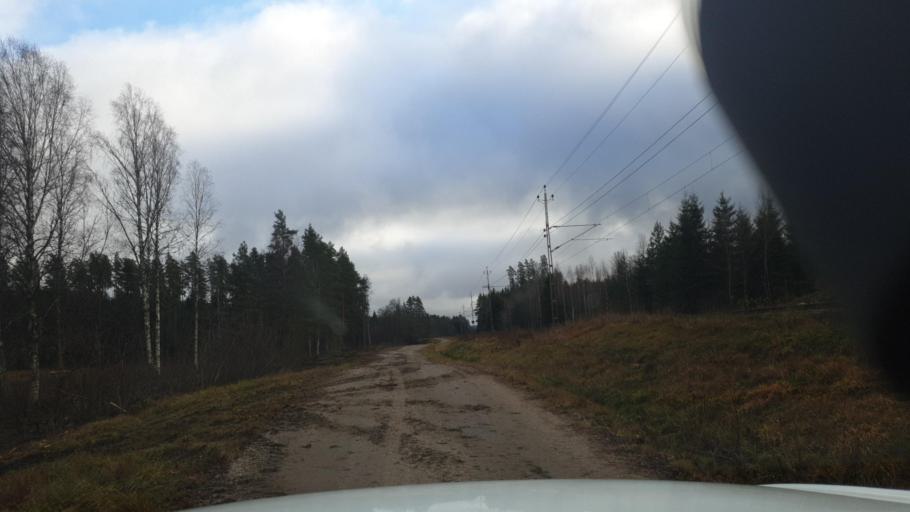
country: SE
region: Vaermland
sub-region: Karlstads Kommun
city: Edsvalla
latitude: 59.6158
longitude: 12.9683
